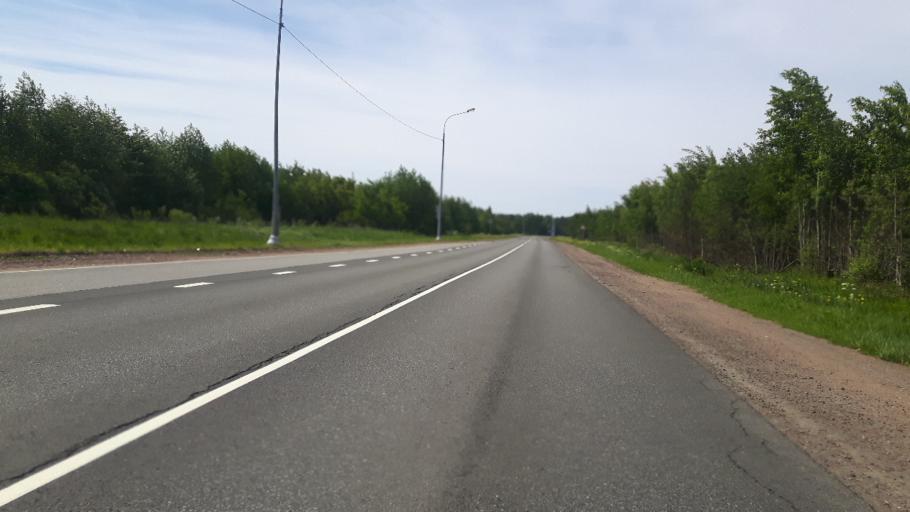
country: RU
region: Leningrad
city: Ust'-Luga
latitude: 59.6538
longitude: 28.3776
